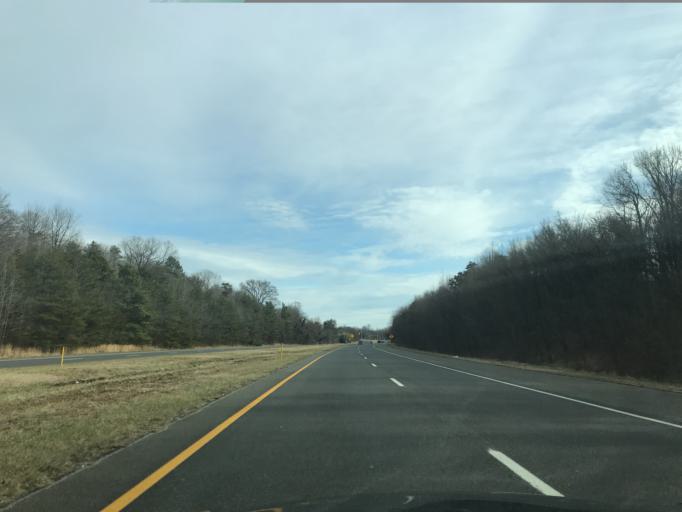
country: US
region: Maryland
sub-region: Prince George's County
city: Glenn Dale
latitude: 38.9811
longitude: -76.8065
